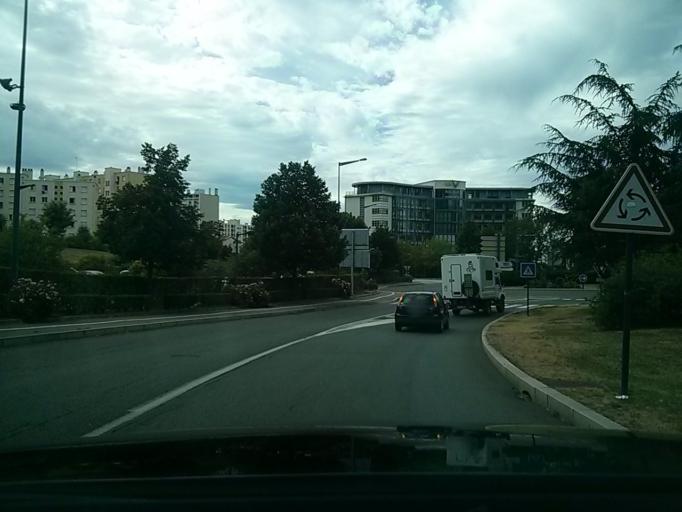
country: FR
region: Rhone-Alpes
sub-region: Departement de la Loire
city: Saint-Etienne
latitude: 45.4099
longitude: 4.3990
